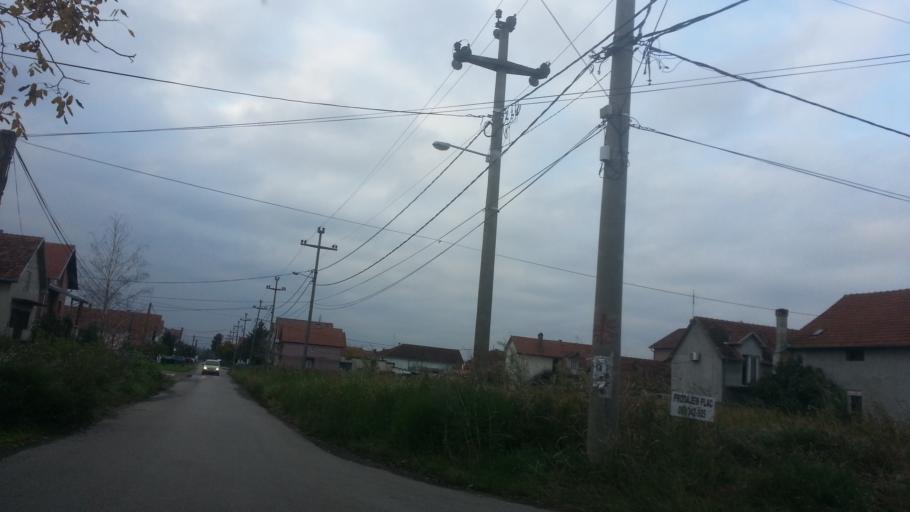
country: RS
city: Novi Banovci
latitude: 44.9110
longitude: 20.2723
